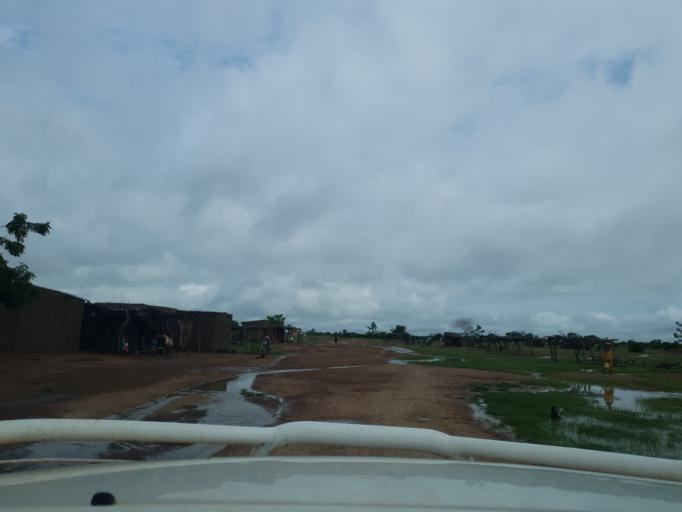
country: ML
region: Segou
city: Bla
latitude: 12.8055
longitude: -5.6060
